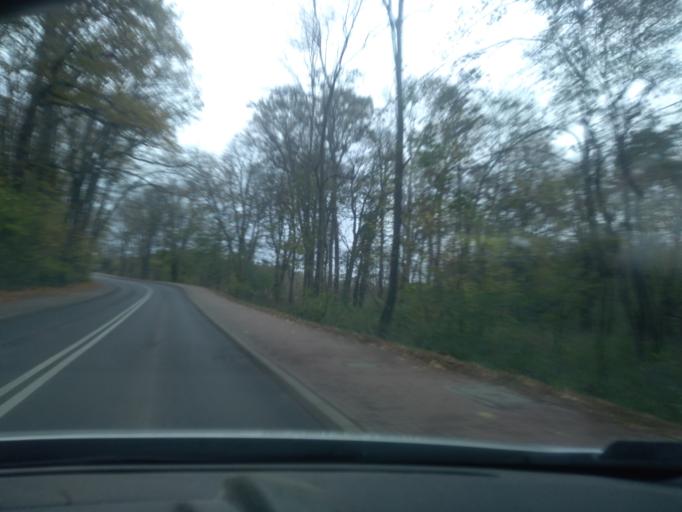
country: PL
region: Greater Poland Voivodeship
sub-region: Powiat poznanski
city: Murowana Goslina
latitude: 52.5423
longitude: 16.9530
